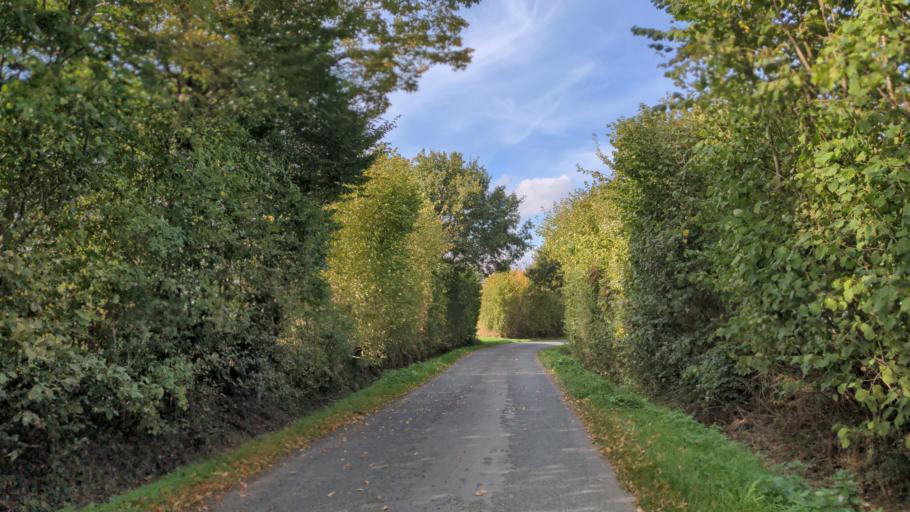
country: DE
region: Schleswig-Holstein
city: Monkhagen
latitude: 53.9286
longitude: 10.5751
